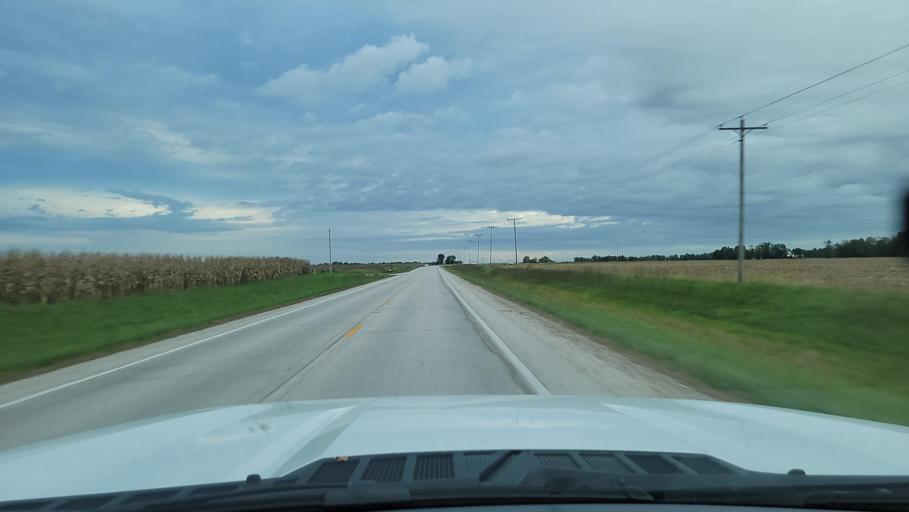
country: US
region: Illinois
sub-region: Schuyler County
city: Rushville
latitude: 40.0704
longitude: -90.6152
